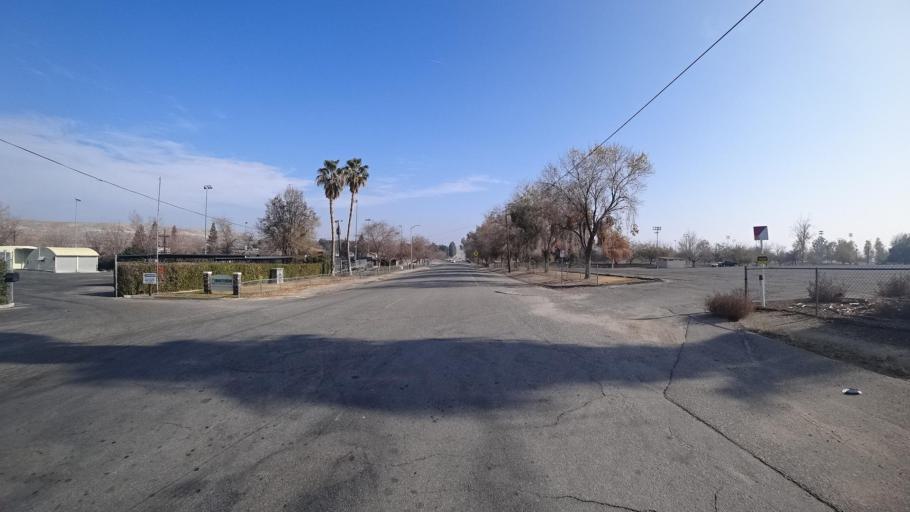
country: US
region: California
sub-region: Kern County
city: Ford City
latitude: 35.1549
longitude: -119.4430
